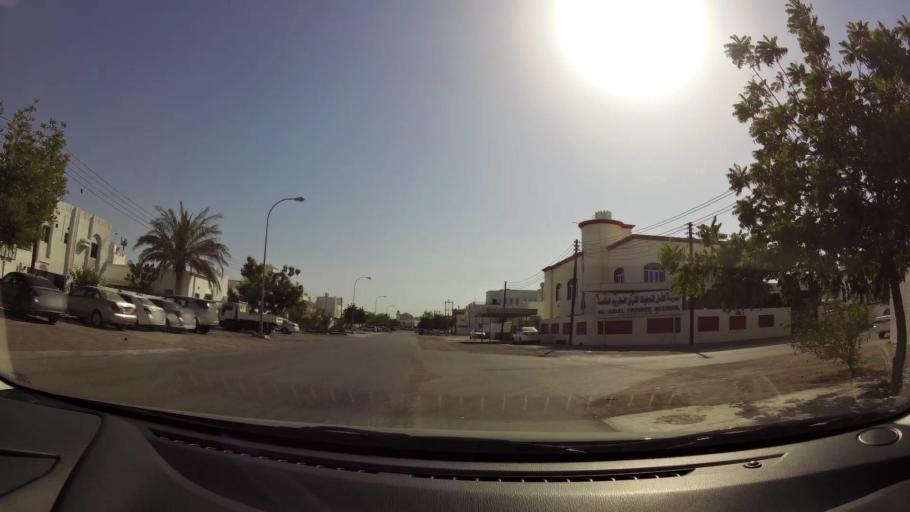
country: OM
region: Muhafazat Masqat
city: As Sib al Jadidah
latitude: 23.6307
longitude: 58.2057
